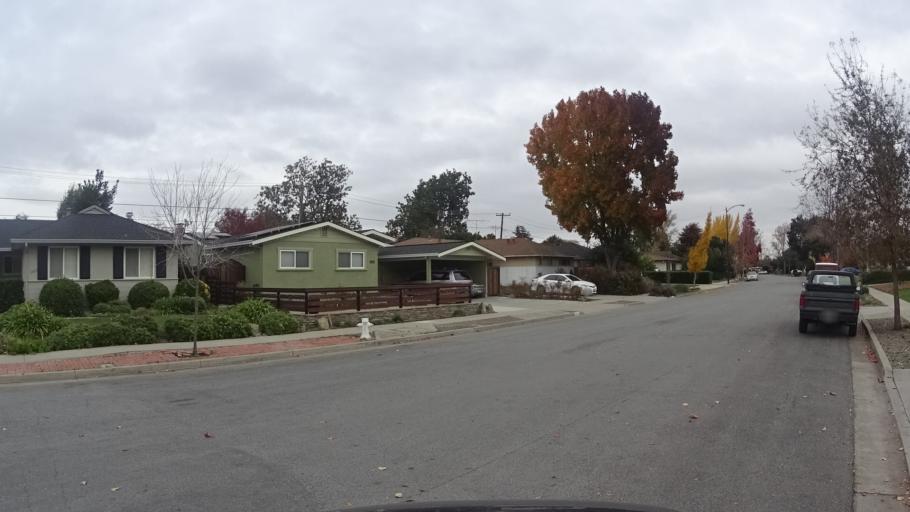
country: US
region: California
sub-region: Santa Clara County
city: Sunnyvale
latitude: 37.3672
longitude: -122.0610
